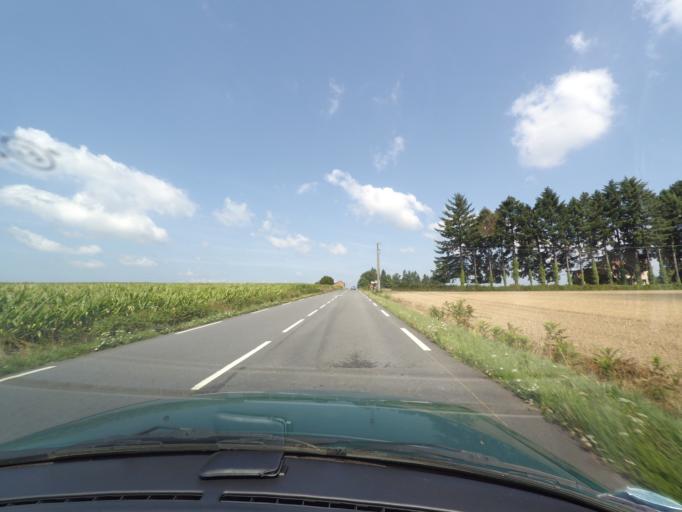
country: FR
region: Limousin
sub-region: Departement de la Haute-Vienne
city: Neuvic-Entier
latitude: 45.7504
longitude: 1.5979
